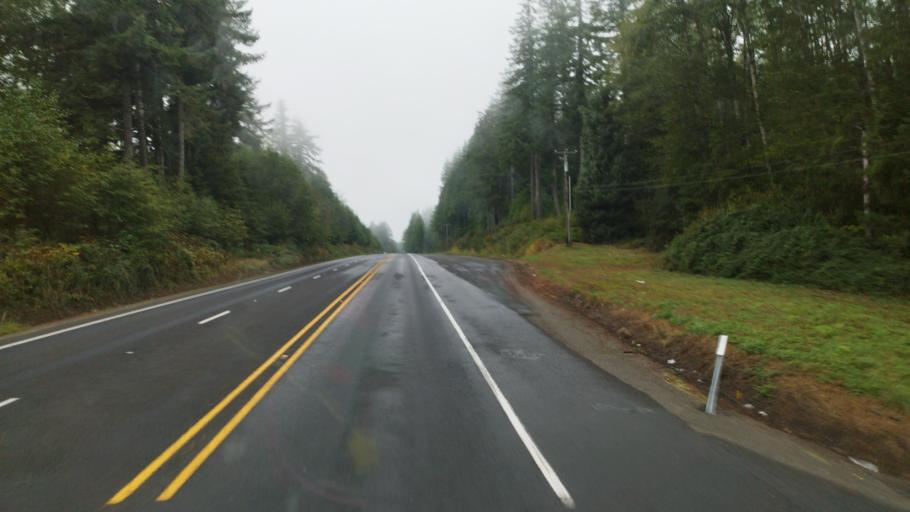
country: US
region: Washington
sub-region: Wahkiakum County
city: Cathlamet
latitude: 46.1693
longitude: -123.4564
